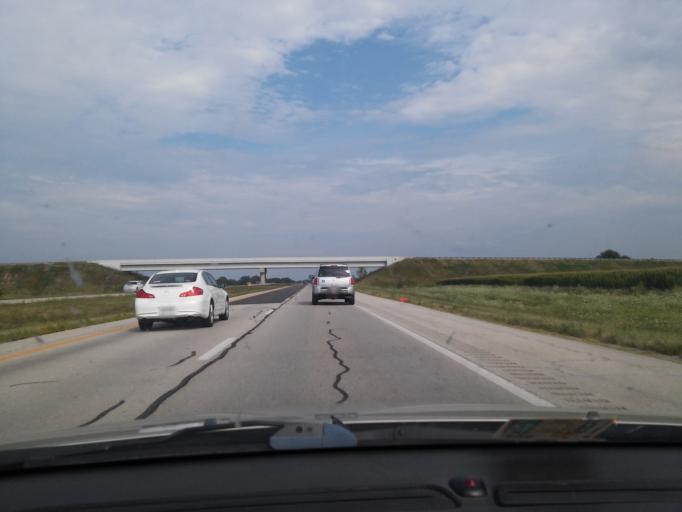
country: US
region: Ohio
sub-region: Fayette County
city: Jeffersonville
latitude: 39.5881
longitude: -83.5519
